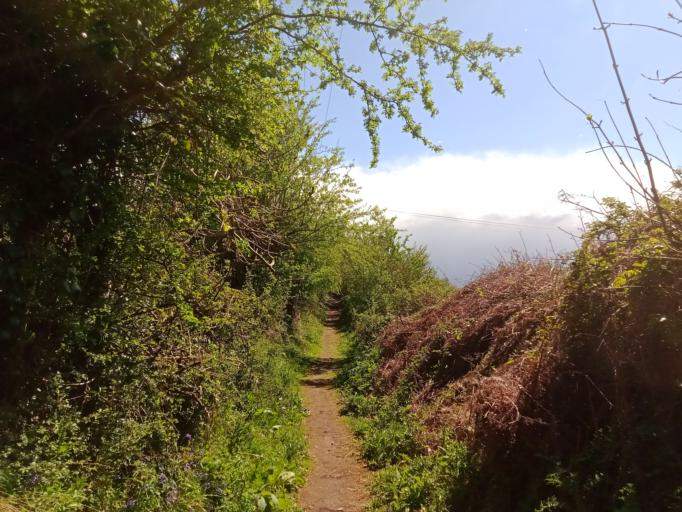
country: IE
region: Leinster
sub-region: Kilkenny
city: Kilkenny
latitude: 52.6924
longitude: -7.2661
